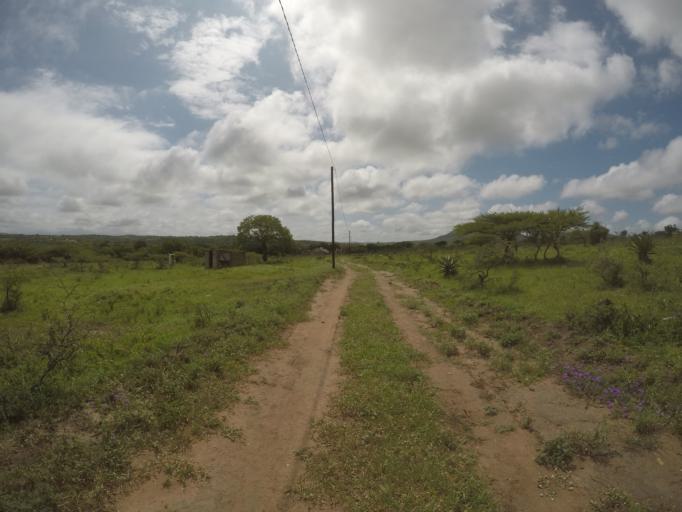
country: ZA
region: KwaZulu-Natal
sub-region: uThungulu District Municipality
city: Empangeni
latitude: -28.5716
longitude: 31.8438
